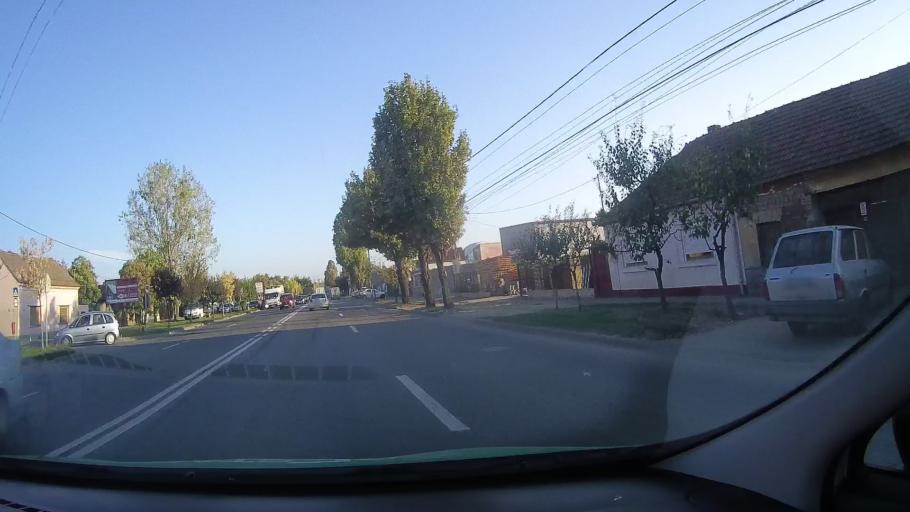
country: RO
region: Bihor
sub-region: Comuna Biharea
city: Oradea
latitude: 47.0931
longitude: 21.9051
